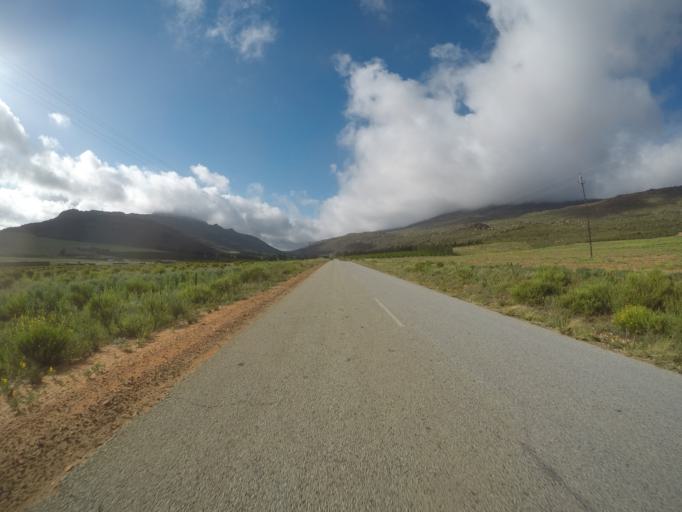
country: ZA
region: Western Cape
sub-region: West Coast District Municipality
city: Clanwilliam
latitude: -32.3526
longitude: 18.8491
